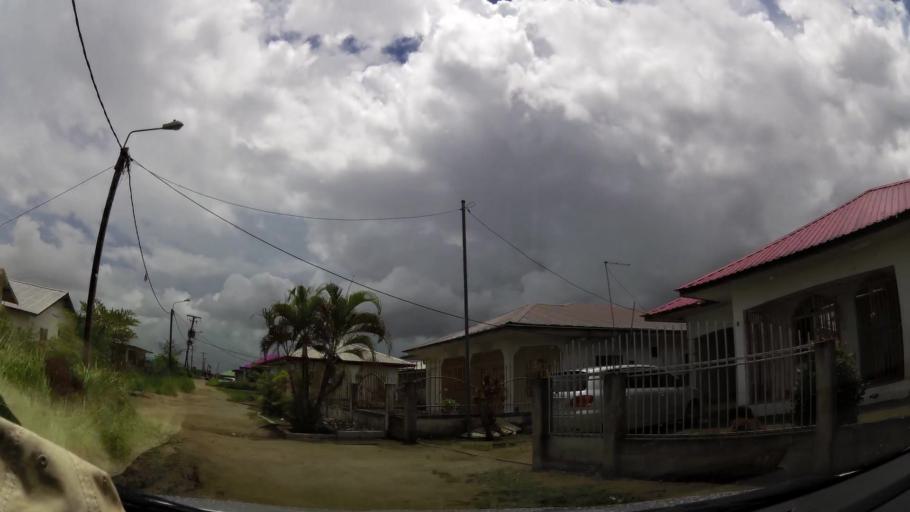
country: SR
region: Wanica
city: Lelydorp
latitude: 5.7894
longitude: -55.2210
